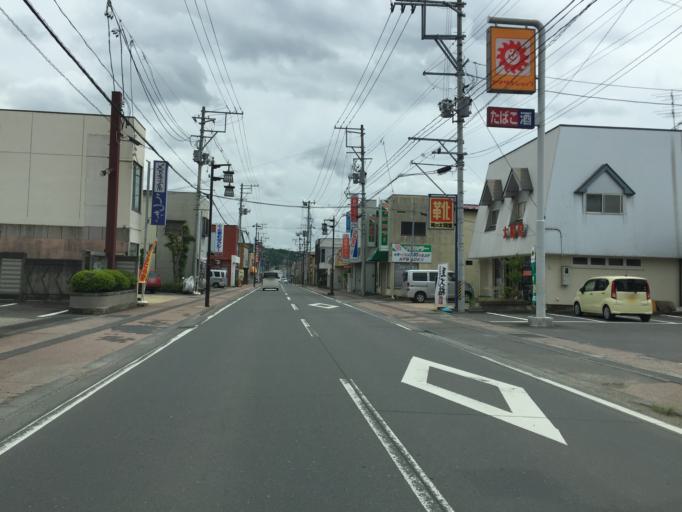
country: JP
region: Fukushima
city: Ishikawa
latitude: 37.0295
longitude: 140.3883
